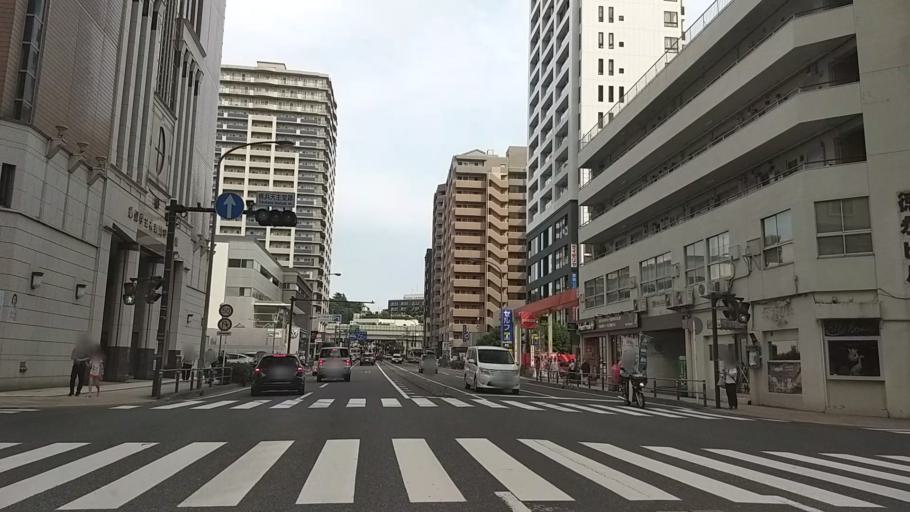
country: JP
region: Kanagawa
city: Yokohama
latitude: 35.4437
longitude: 139.6486
